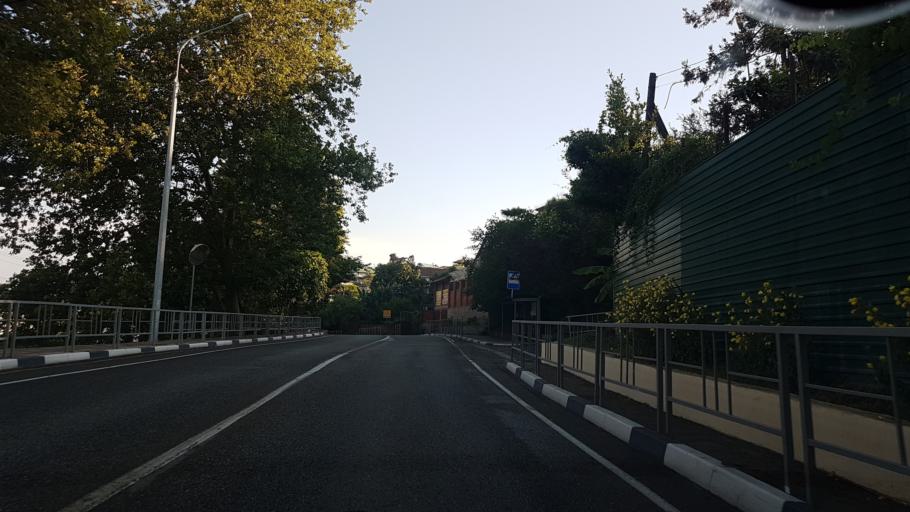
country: RU
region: Krasnodarskiy
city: Gornoye Loo
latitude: 43.6931
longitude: 39.5914
